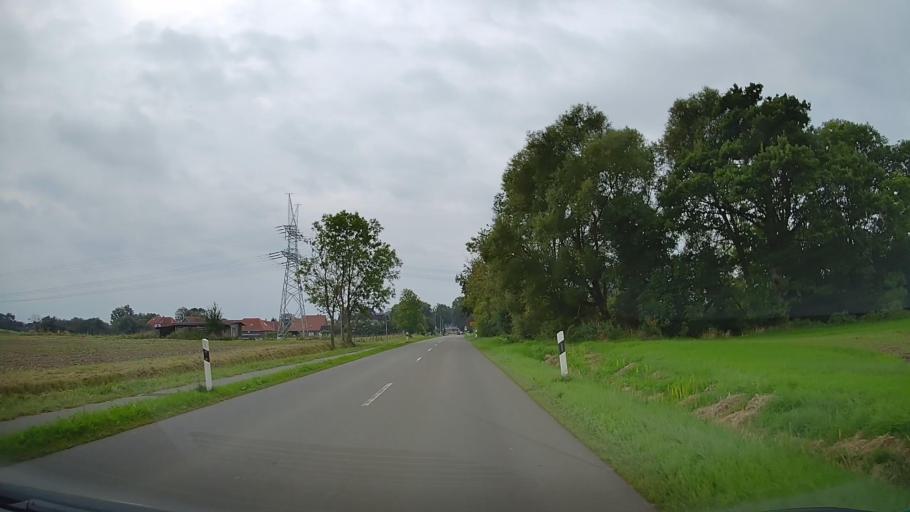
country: DE
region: Lower Saxony
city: Stade
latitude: 53.6209
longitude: 9.4628
